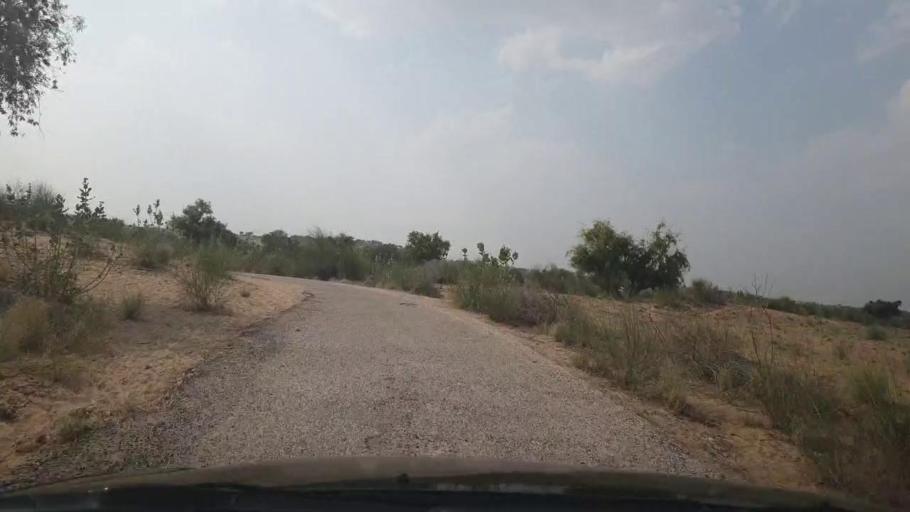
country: PK
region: Sindh
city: Islamkot
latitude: 24.9663
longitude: 70.6195
